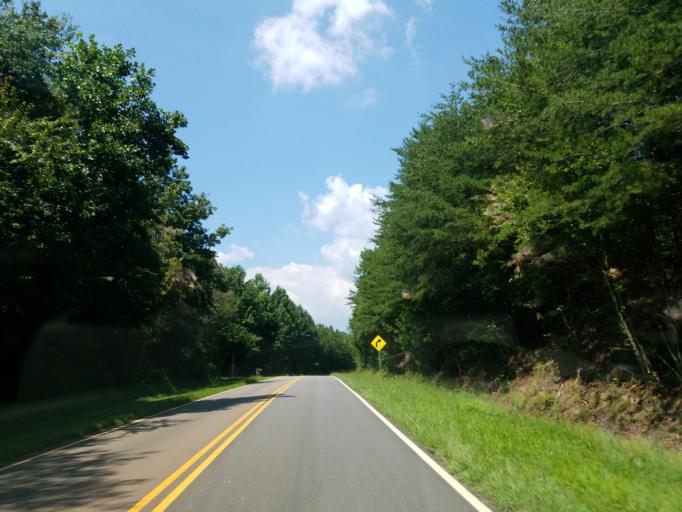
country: US
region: Georgia
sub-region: Lumpkin County
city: Dahlonega
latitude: 34.6077
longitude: -83.8985
